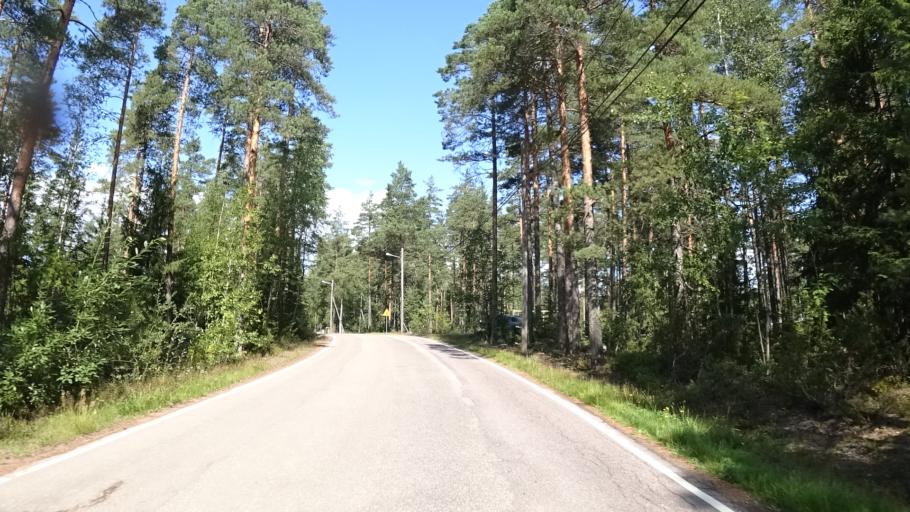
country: FI
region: Kymenlaakso
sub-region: Kotka-Hamina
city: Karhula
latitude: 60.5566
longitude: 26.9008
